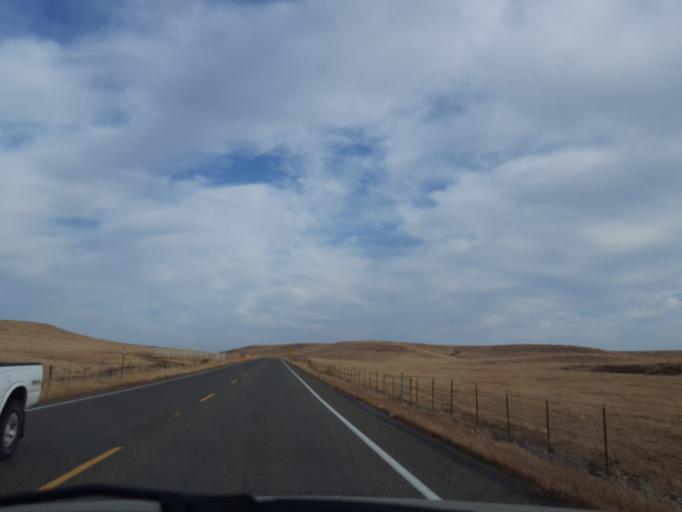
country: US
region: California
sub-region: Merced County
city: Merced
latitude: 37.4577
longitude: -120.4359
